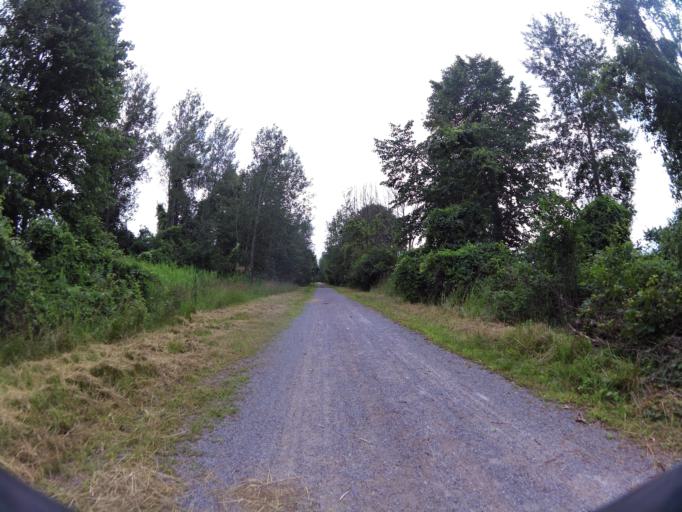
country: CA
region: Ontario
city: Bells Corners
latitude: 45.1519
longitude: -75.6131
